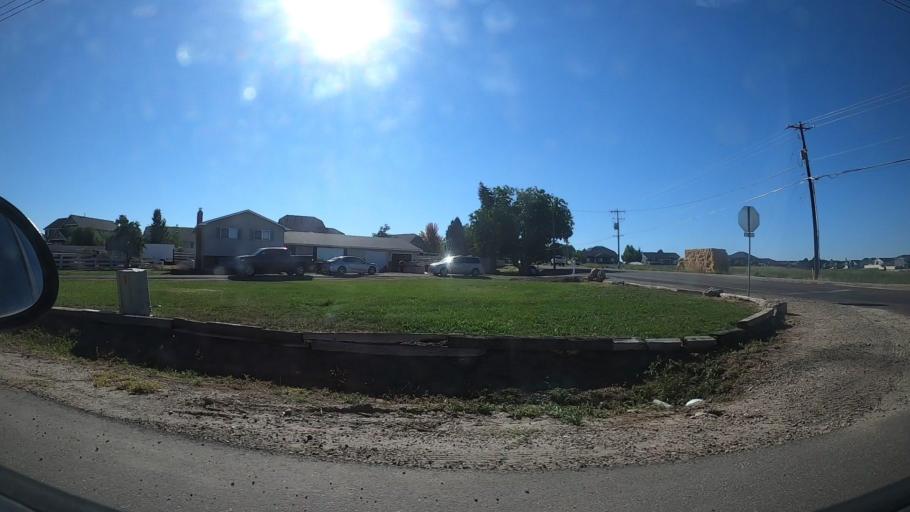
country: US
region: Idaho
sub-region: Canyon County
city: Nampa
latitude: 43.5557
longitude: -116.6128
